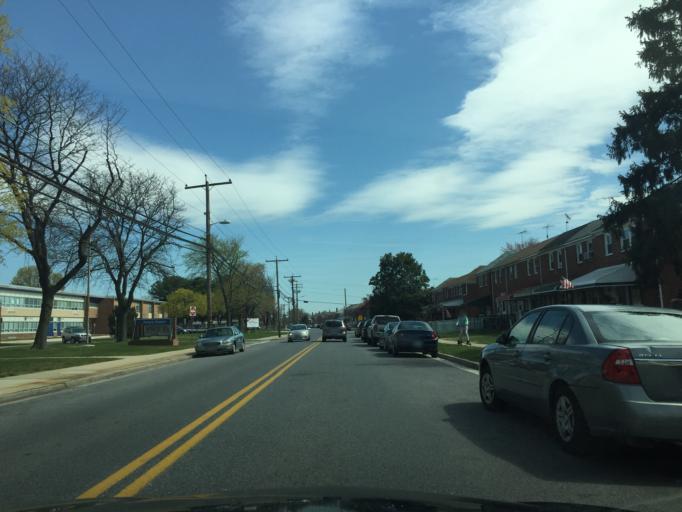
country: US
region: Maryland
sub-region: Baltimore County
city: Middle River
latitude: 39.3265
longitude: -76.4383
